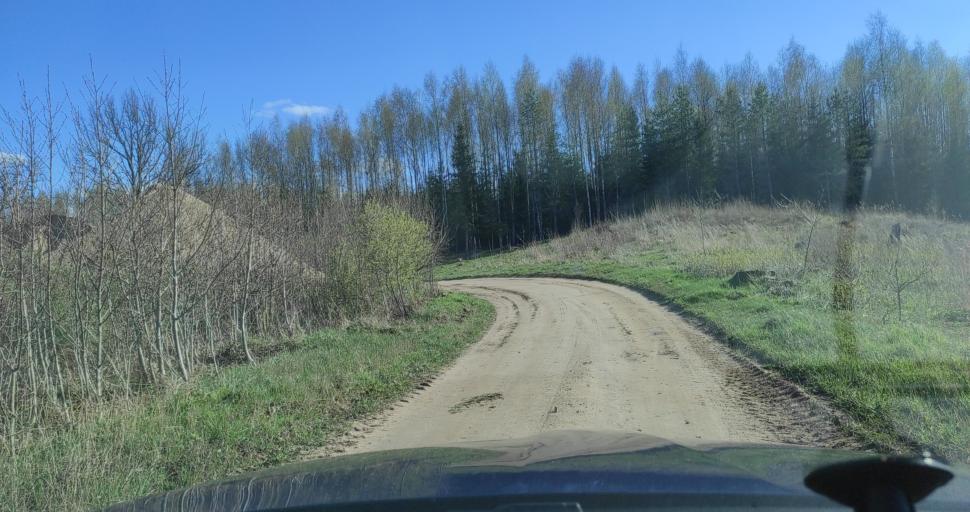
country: LV
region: Kuldigas Rajons
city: Kuldiga
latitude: 56.8981
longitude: 21.8574
